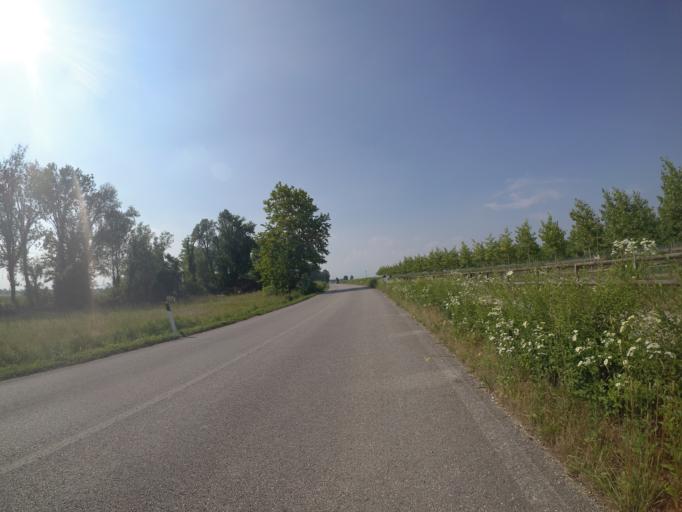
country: IT
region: Friuli Venezia Giulia
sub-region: Provincia di Udine
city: Camino al Tagliamento
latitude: 45.9242
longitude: 12.9637
